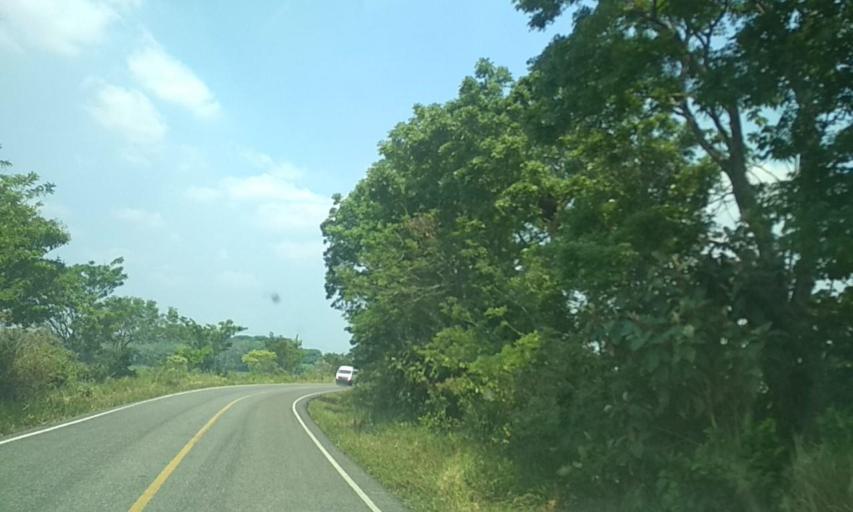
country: MX
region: Tabasco
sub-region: Huimanguillo
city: C-41 (Licenciado Carlos A. Madrazo)
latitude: 17.8494
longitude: -93.5338
